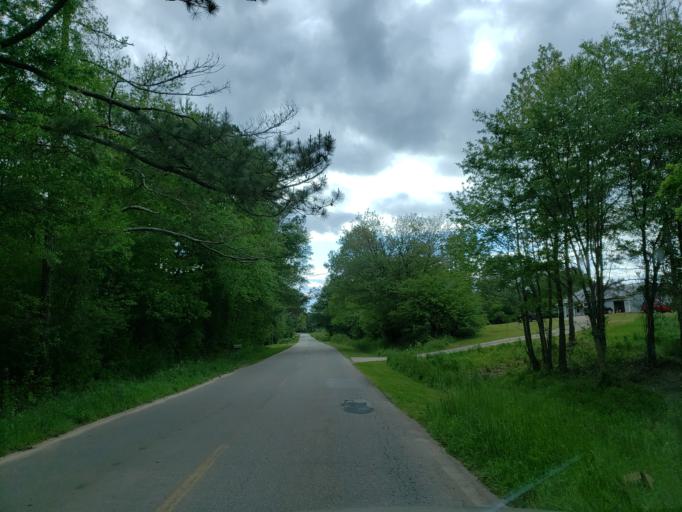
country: US
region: Georgia
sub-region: Haralson County
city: Tallapoosa
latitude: 33.7742
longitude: -85.3528
